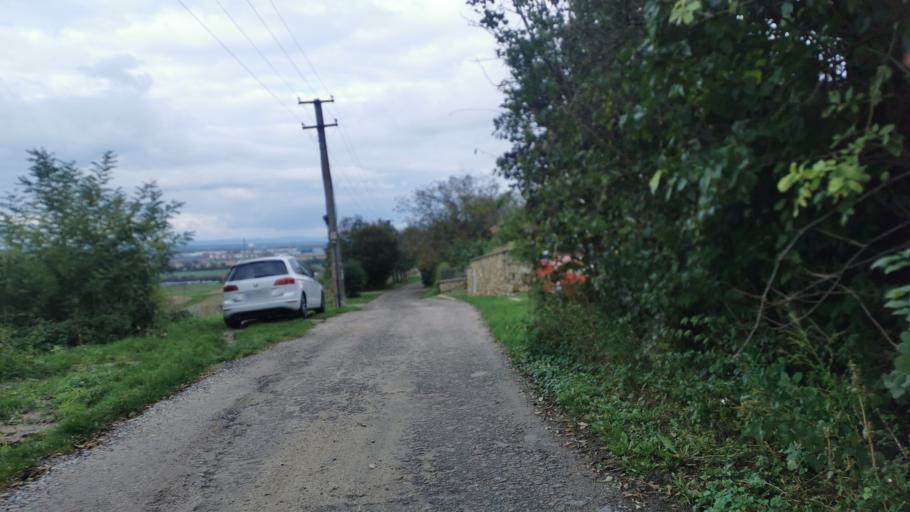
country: SK
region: Trnavsky
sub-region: Okres Skalica
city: Skalica
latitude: 48.8180
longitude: 17.2192
